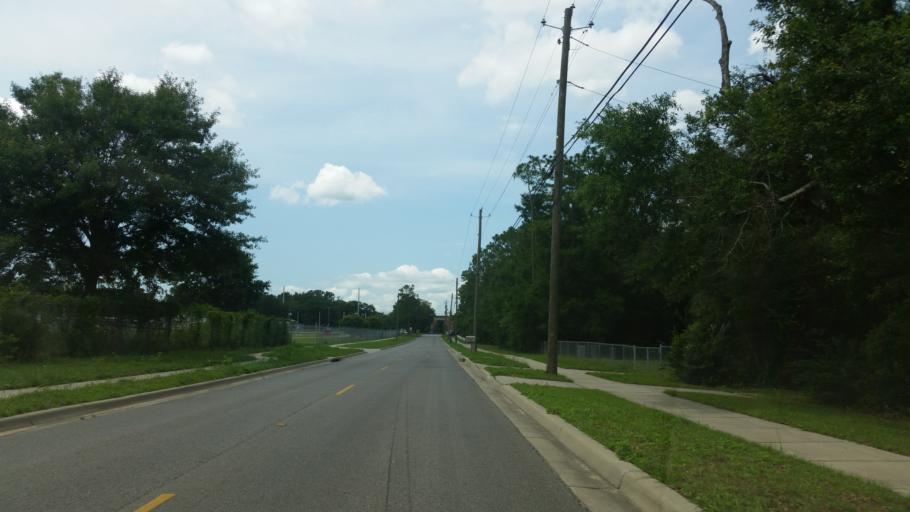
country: US
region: Florida
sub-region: Escambia County
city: Ensley
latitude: 30.5297
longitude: -87.2498
